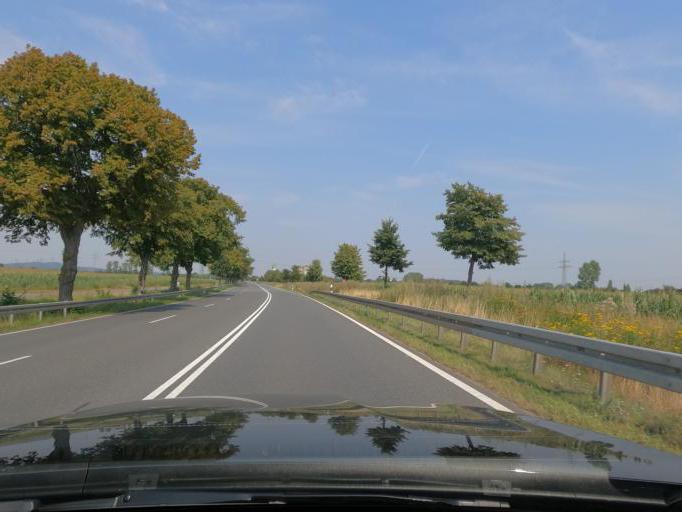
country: DE
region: Lower Saxony
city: Gehrden
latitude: 52.2843
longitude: 9.6286
